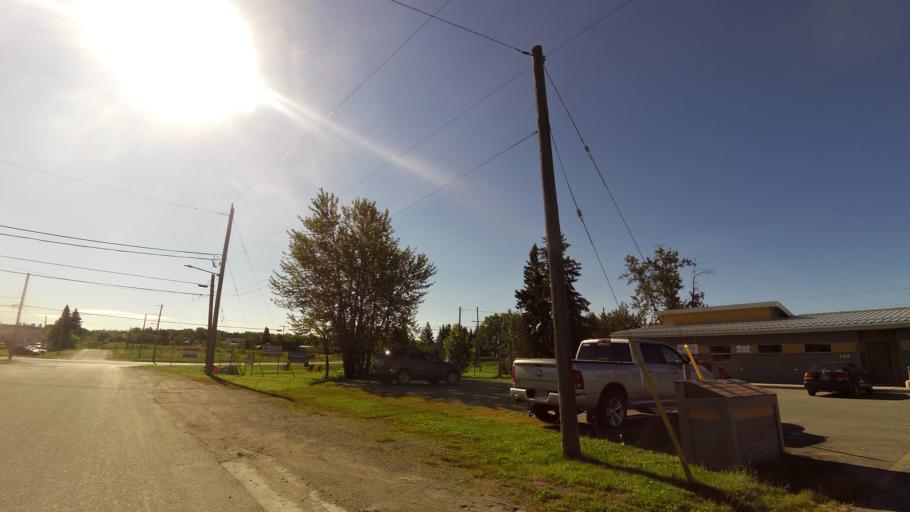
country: CA
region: Ontario
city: Iroquois Falls
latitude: 48.5347
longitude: -80.4653
